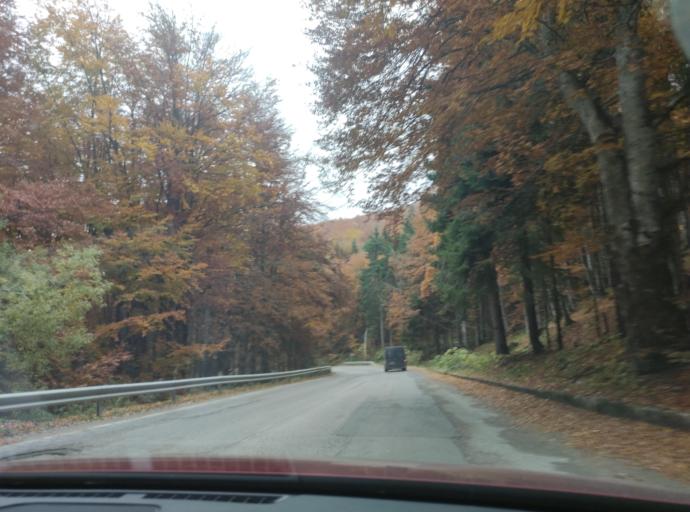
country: BG
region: Montana
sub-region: Obshtina Berkovitsa
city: Berkovitsa
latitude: 43.1239
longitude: 23.1309
